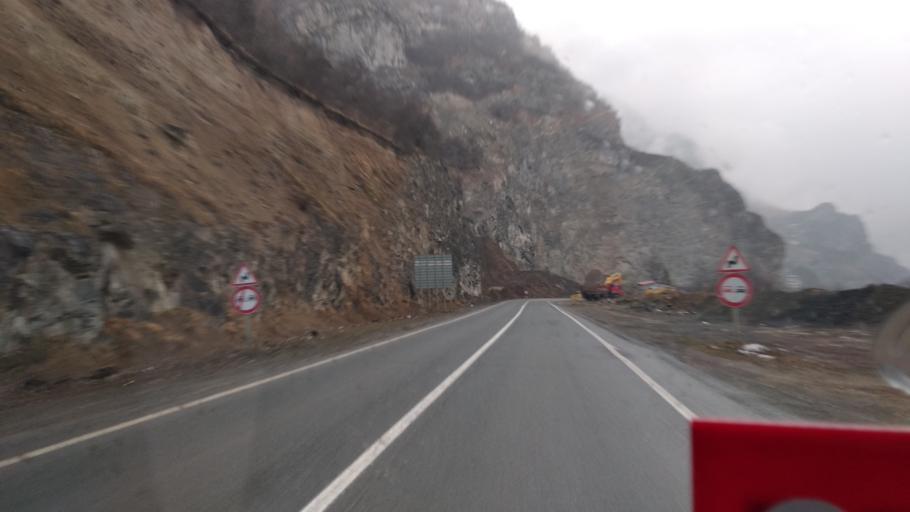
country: TR
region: Trabzon
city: Macka
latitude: 40.7216
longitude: 39.5186
